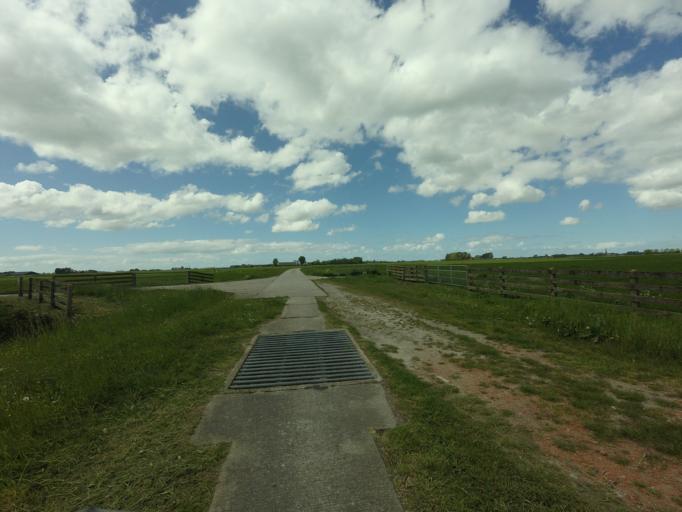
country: NL
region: Friesland
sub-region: Gemeente Franekeradeel
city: Tzum
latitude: 53.1290
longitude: 5.5622
